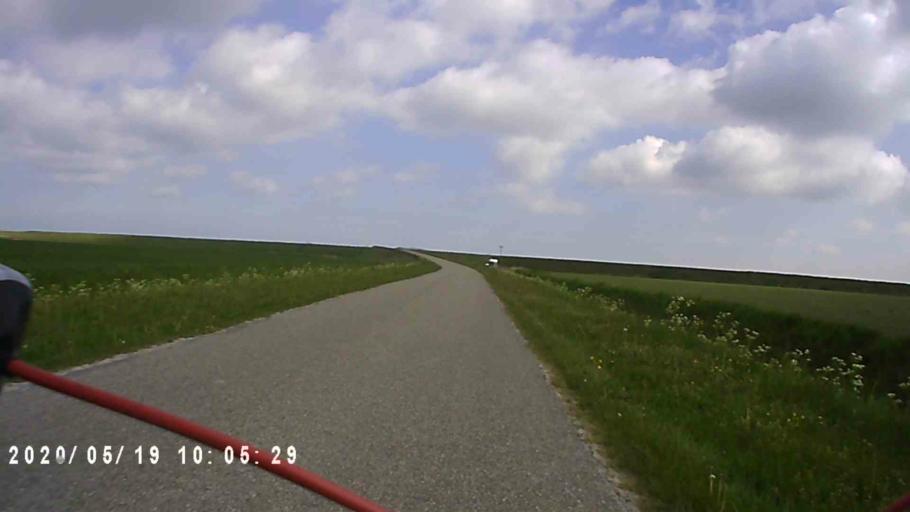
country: NL
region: Friesland
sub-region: Gemeente Kollumerland en Nieuwkruisland
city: Kollum
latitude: 53.3099
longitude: 6.2279
